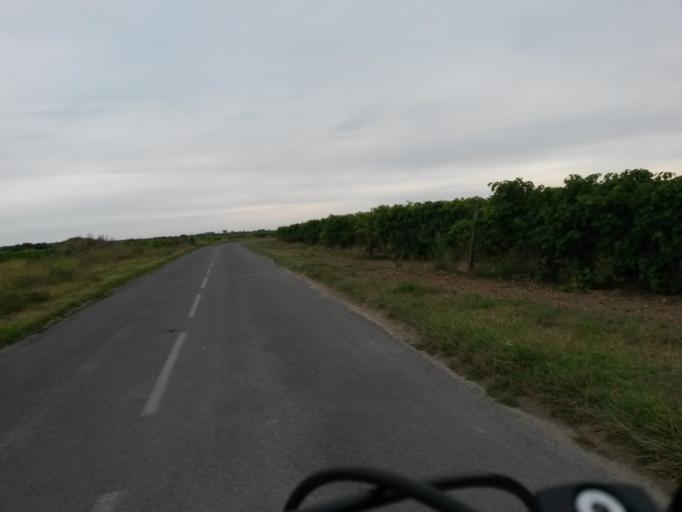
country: FR
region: Poitou-Charentes
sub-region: Departement de la Charente-Maritime
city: Dolus-d'Oleron
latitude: 45.9373
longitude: -1.3521
